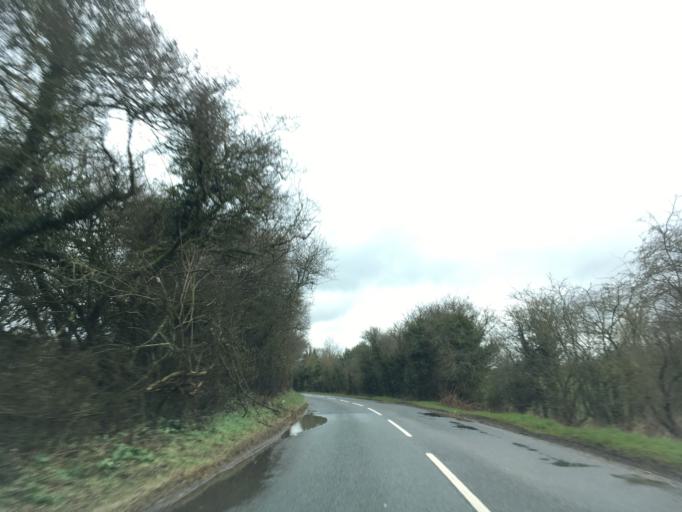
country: GB
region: England
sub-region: Wiltshire
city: Chilton Foliat
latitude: 51.4667
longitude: -1.5294
